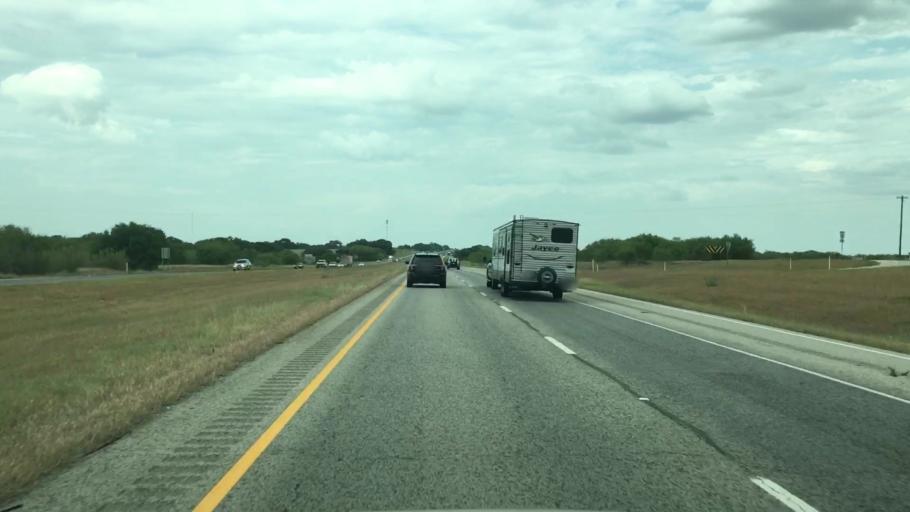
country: US
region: Texas
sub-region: Atascosa County
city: Pleasanton
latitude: 29.1088
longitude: -98.4321
